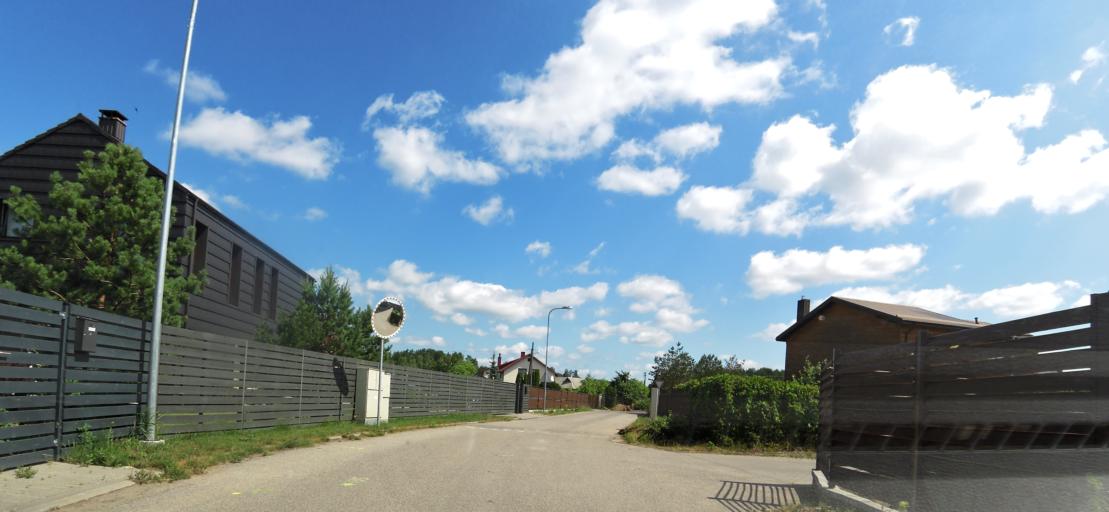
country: LT
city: Nemencine
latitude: 54.8212
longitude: 25.3949
